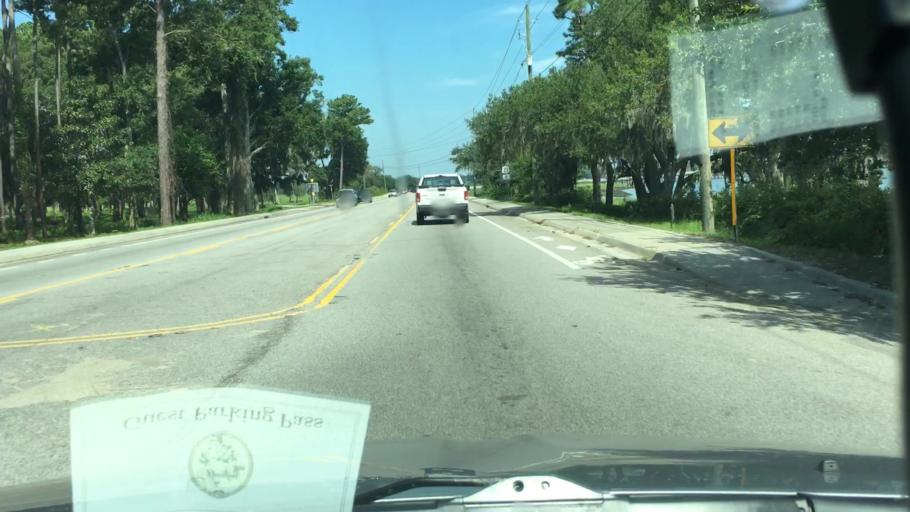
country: US
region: South Carolina
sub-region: Beaufort County
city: Beaufort
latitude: 32.4203
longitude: -80.6631
